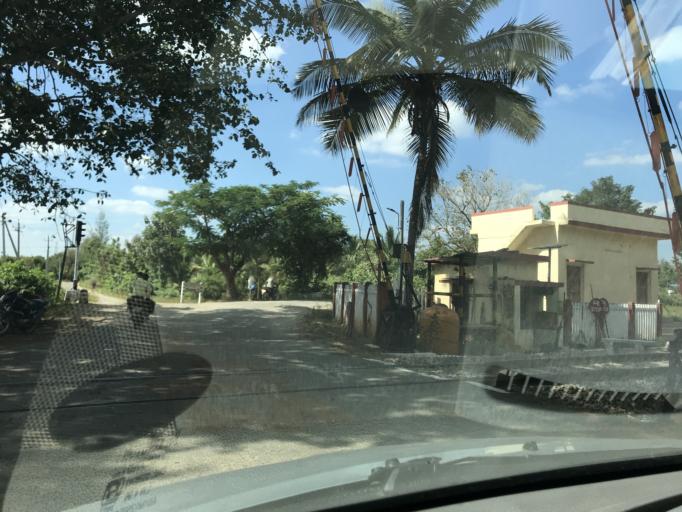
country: IN
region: Karnataka
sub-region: Mandya
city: Krishnarajpet
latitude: 12.6396
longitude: 76.3807
